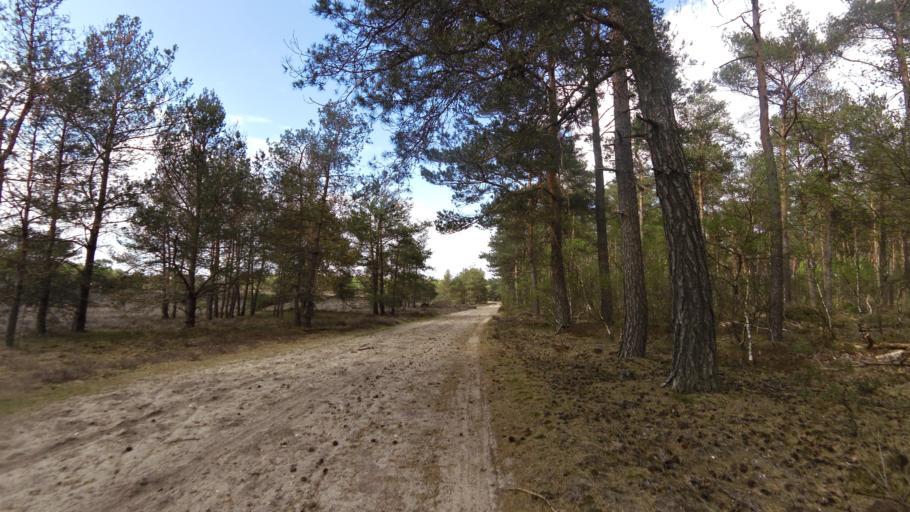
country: NL
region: Gelderland
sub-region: Gemeente Apeldoorn
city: Loenen
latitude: 52.0795
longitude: 6.0114
